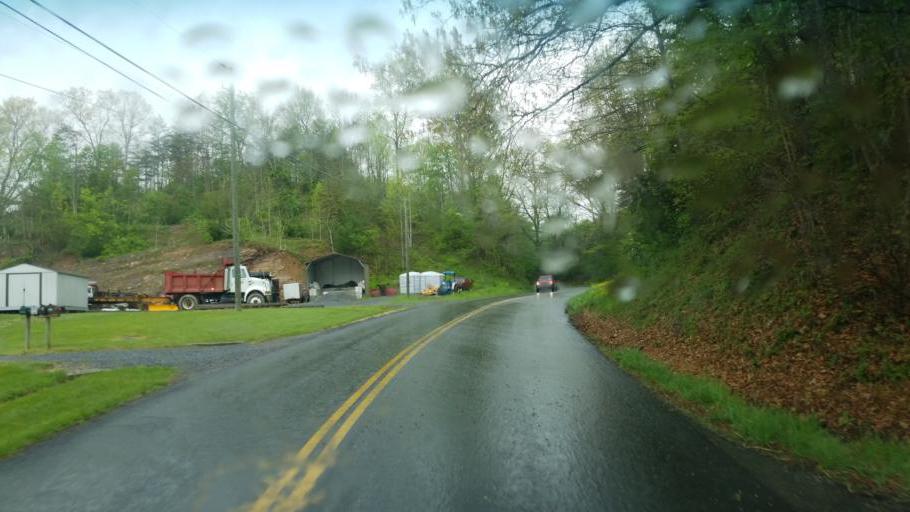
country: US
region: Virginia
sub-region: Smyth County
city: Adwolf
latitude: 36.7795
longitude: -81.5745
